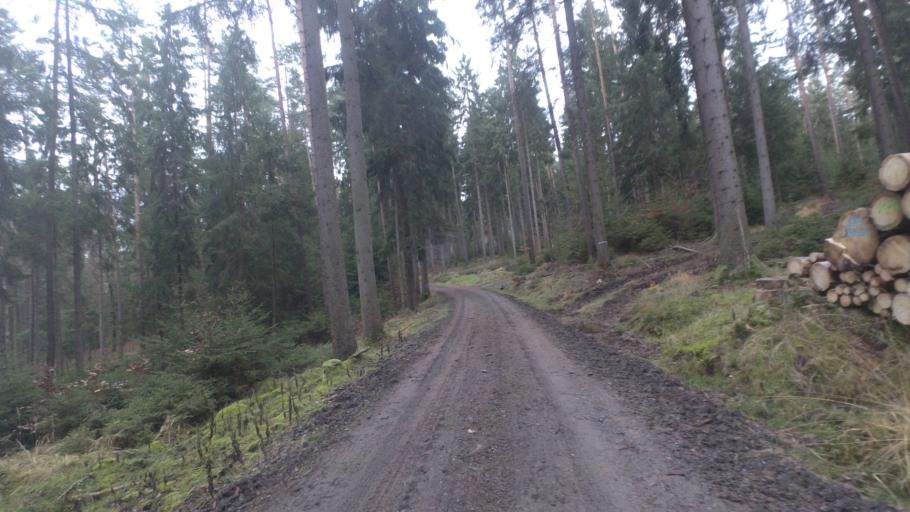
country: DE
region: Thuringia
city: Herschdorf
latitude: 50.7024
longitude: 11.4959
